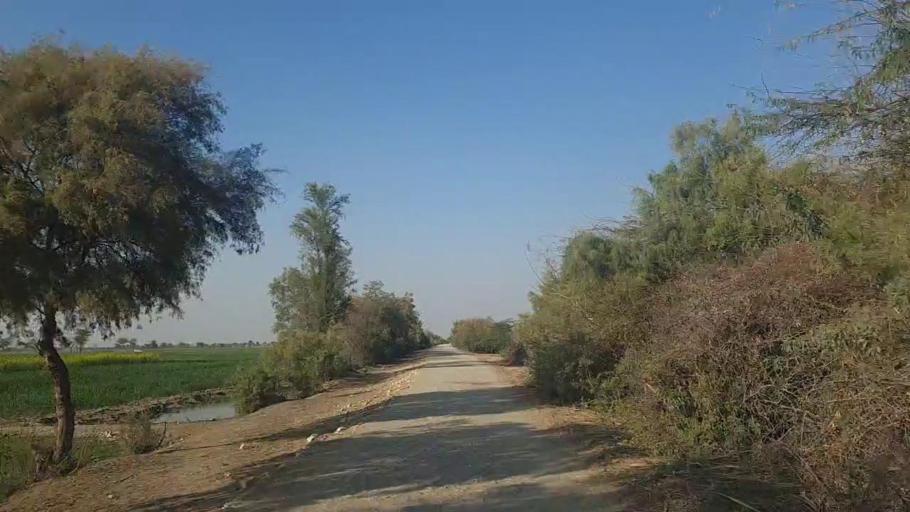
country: PK
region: Sindh
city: Jam Sahib
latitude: 26.3241
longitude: 68.7146
